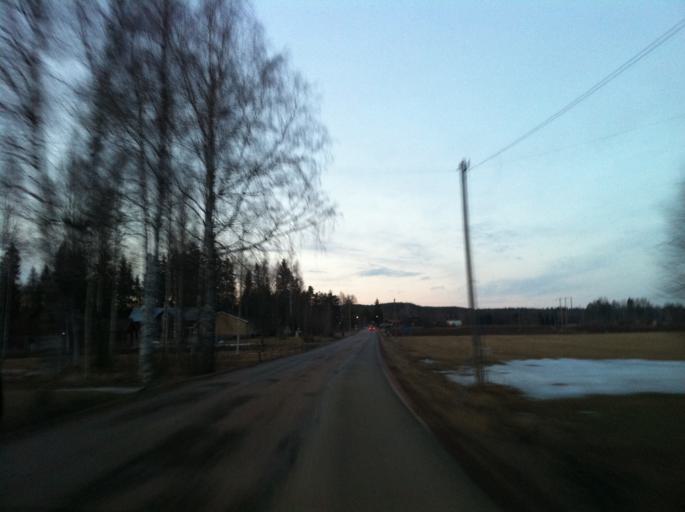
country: SE
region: Dalarna
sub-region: Orsa Kommun
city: Orsa
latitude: 61.1322
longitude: 14.5980
